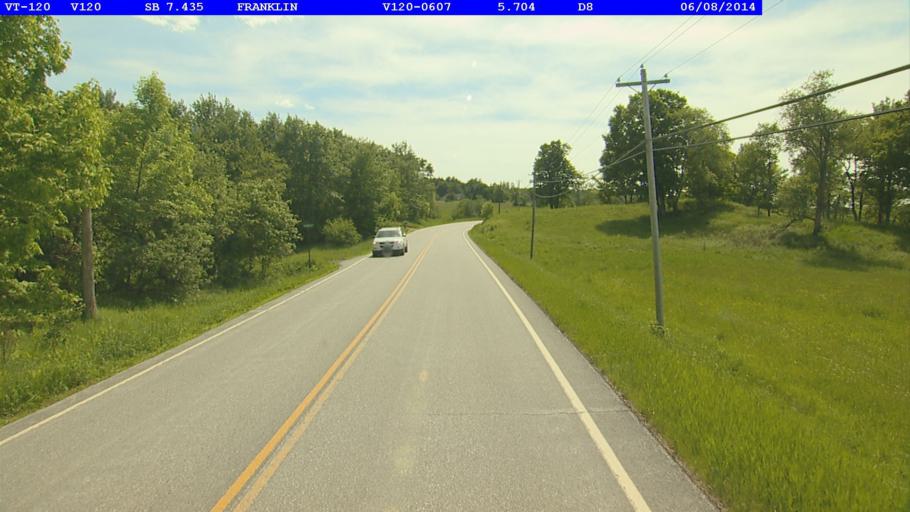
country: US
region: Vermont
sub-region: Franklin County
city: Enosburg Falls
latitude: 44.9877
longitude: -72.8796
